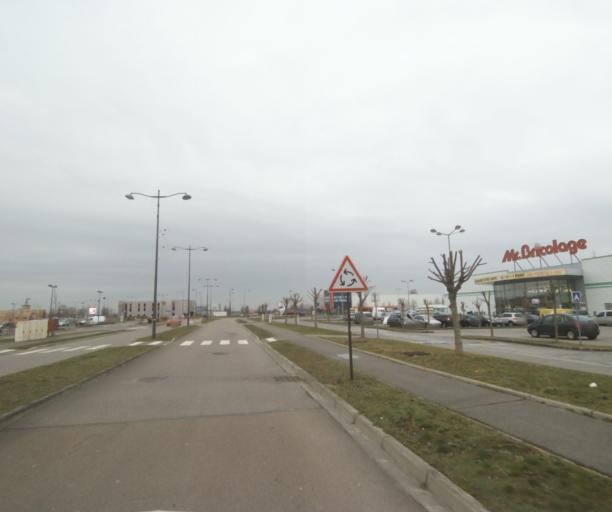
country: FR
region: Champagne-Ardenne
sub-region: Departement de la Haute-Marne
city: Saint-Dizier
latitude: 48.6233
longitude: 4.9663
